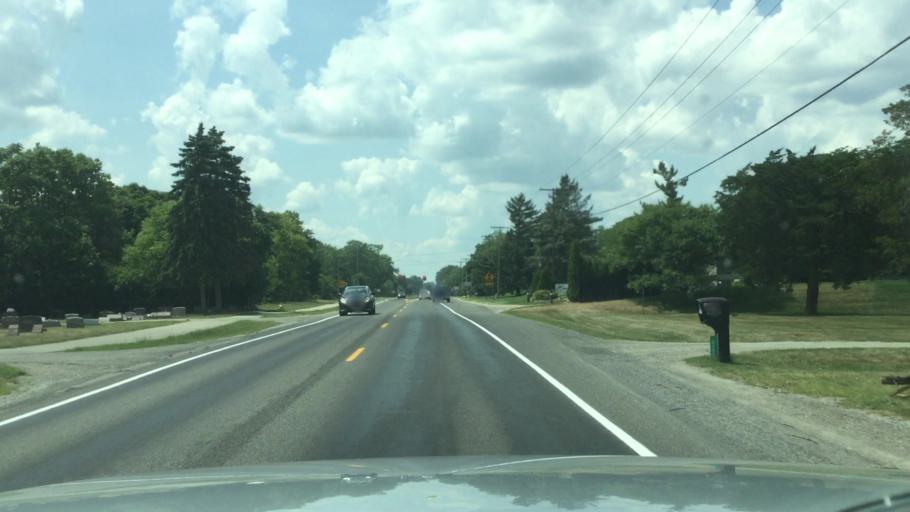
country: US
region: Michigan
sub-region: Washtenaw County
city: Ypsilanti
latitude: 42.2028
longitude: -83.5671
